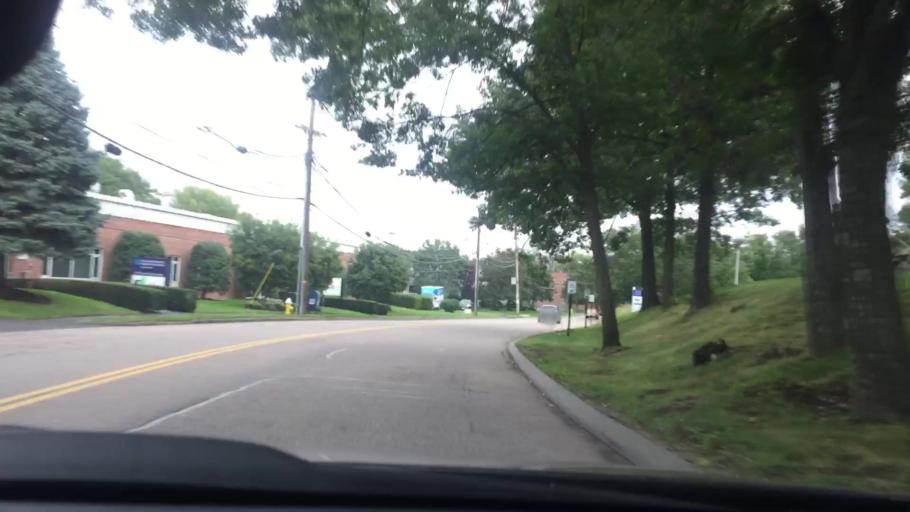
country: US
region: Massachusetts
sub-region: Norfolk County
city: Needham
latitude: 42.3043
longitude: -71.2176
